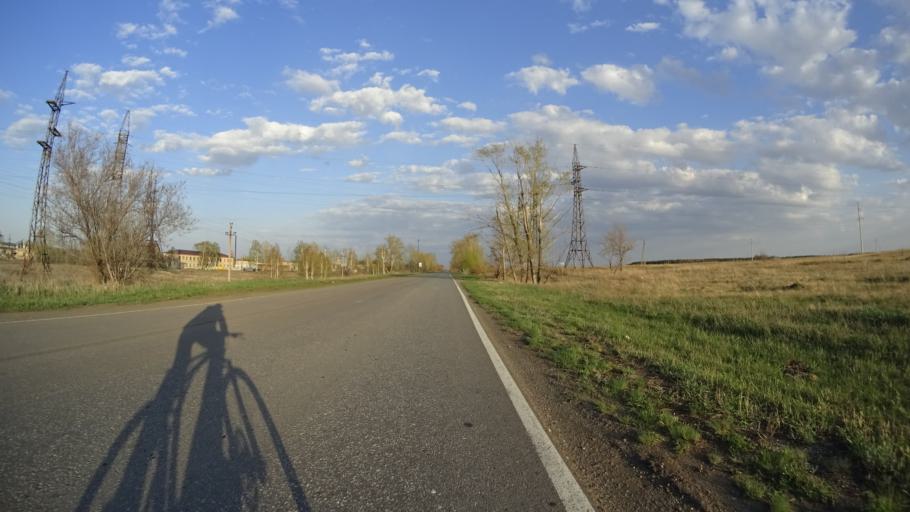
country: RU
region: Chelyabinsk
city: Troitsk
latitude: 54.0572
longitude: 61.5839
